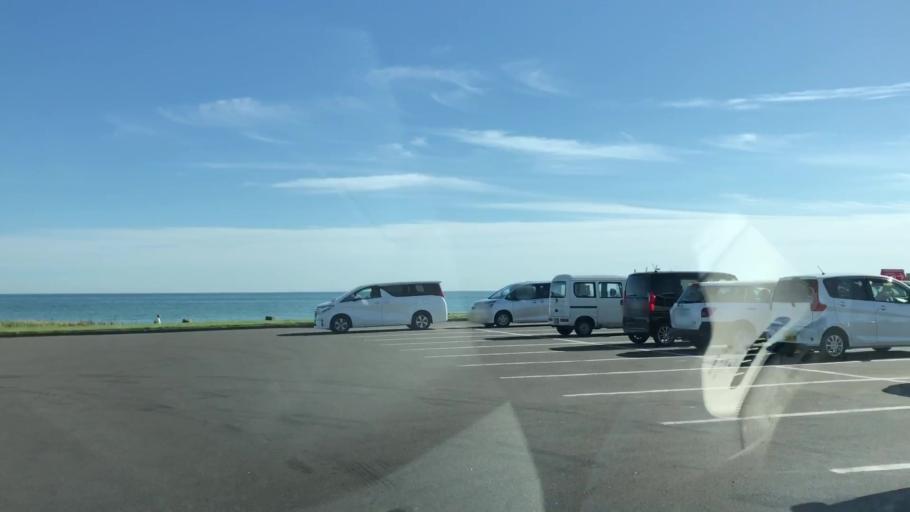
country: JP
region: Hokkaido
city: Kushiro
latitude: 42.9930
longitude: 144.1990
